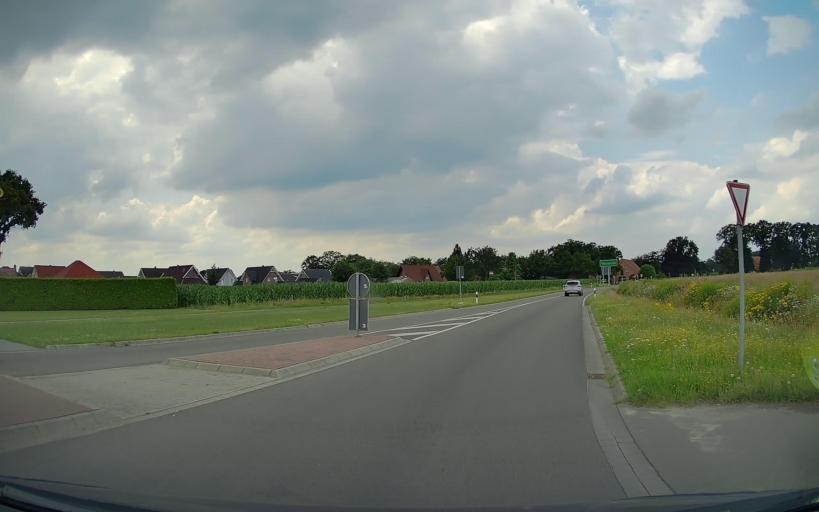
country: DE
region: Lower Saxony
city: Bosel
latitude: 53.0073
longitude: 7.9432
